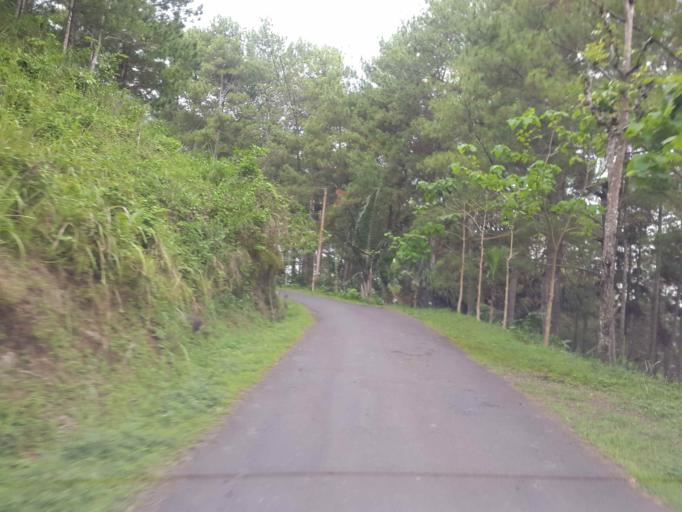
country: ID
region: Central Java
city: Bantarmangu
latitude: -7.3425
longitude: 108.9148
